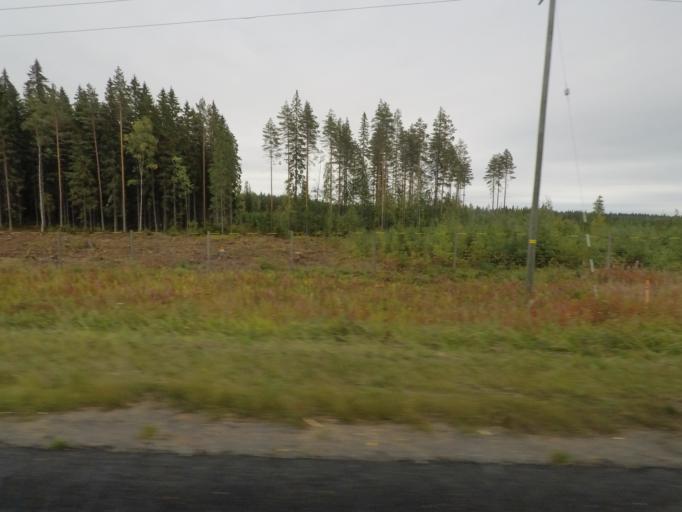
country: FI
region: Southern Savonia
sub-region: Pieksaemaeki
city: Juva
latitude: 61.8039
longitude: 27.6004
